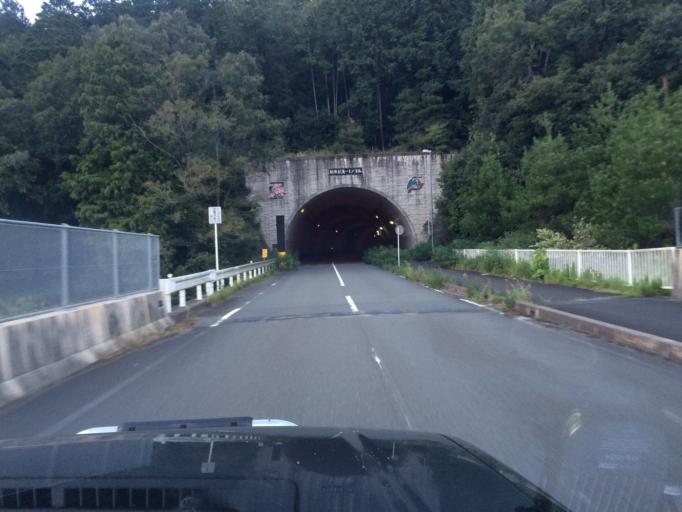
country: JP
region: Kyoto
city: Kameoka
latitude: 35.0850
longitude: 135.4724
